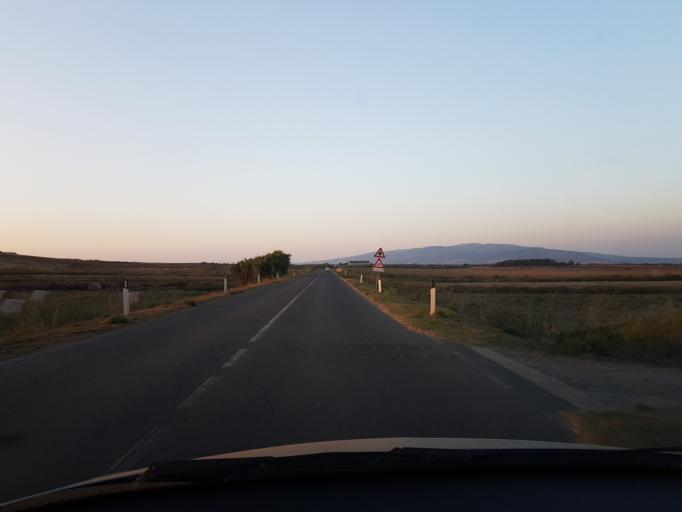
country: IT
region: Sardinia
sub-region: Provincia di Oristano
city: Nurachi
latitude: 39.9744
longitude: 8.4526
